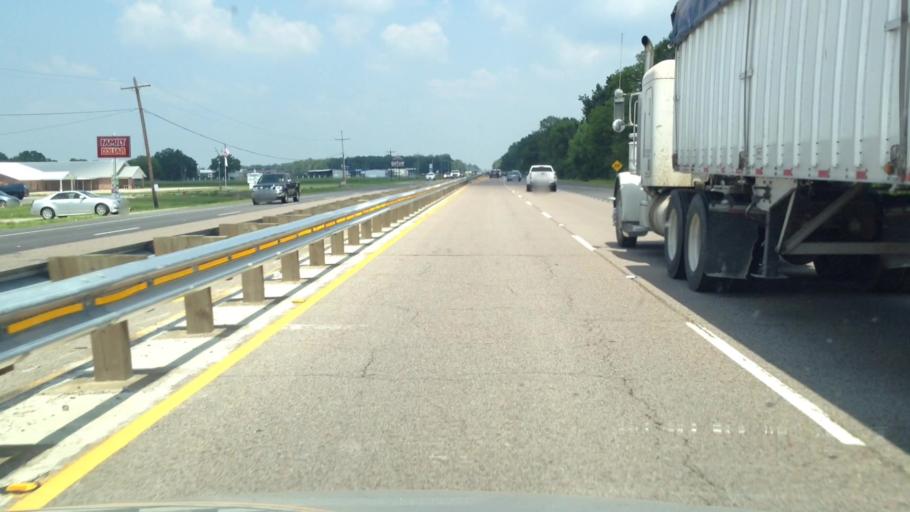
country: US
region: Louisiana
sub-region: Pointe Coupee Parish
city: Livonia
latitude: 30.5545
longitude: -91.5510
